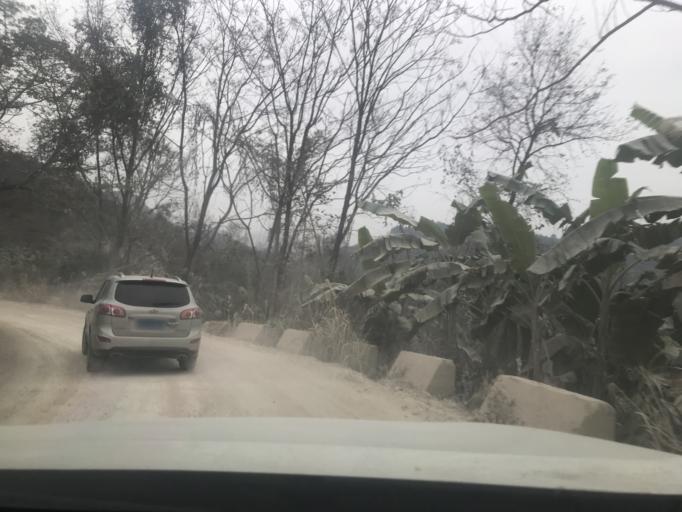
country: CN
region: Guangxi Zhuangzu Zizhiqu
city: Xinzhou
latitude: 25.0058
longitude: 105.8390
